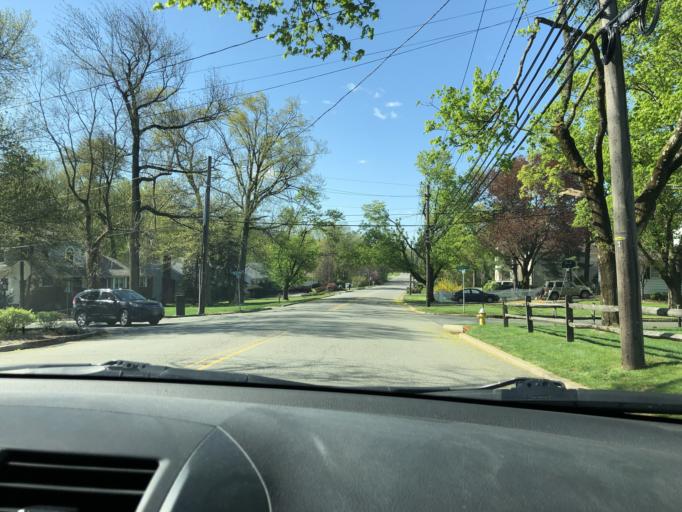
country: US
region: New Jersey
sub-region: Essex County
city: North Caldwell
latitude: 40.8481
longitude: -74.2596
